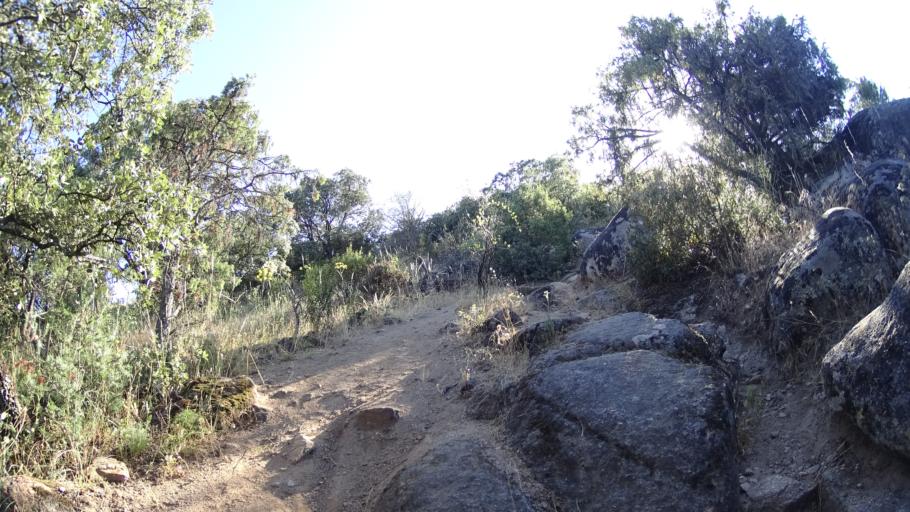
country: ES
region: Madrid
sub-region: Provincia de Madrid
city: Galapagar
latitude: 40.5874
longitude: -3.9724
